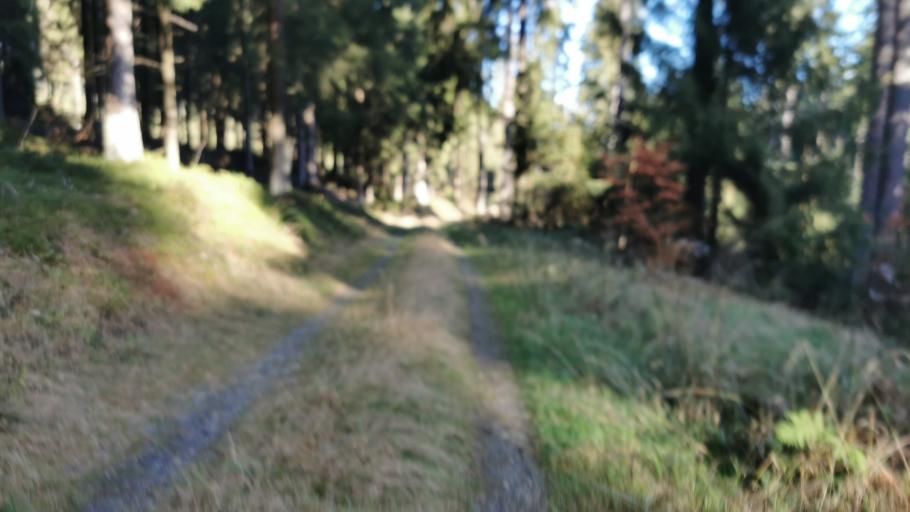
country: DE
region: Bavaria
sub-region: Upper Franconia
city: Reichenbach
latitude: 50.4461
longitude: 11.4285
